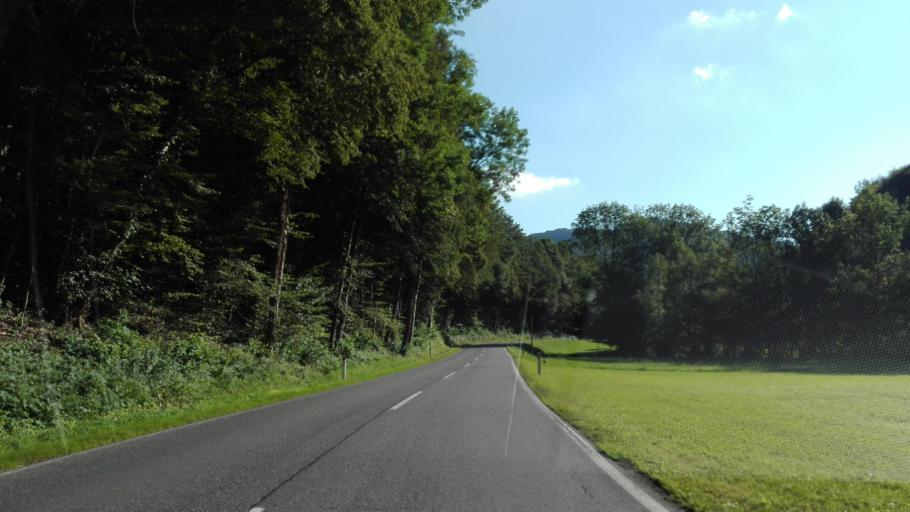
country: AT
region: Lower Austria
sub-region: Politischer Bezirk Sankt Polten
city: Stossing
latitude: 48.0895
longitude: 15.8711
